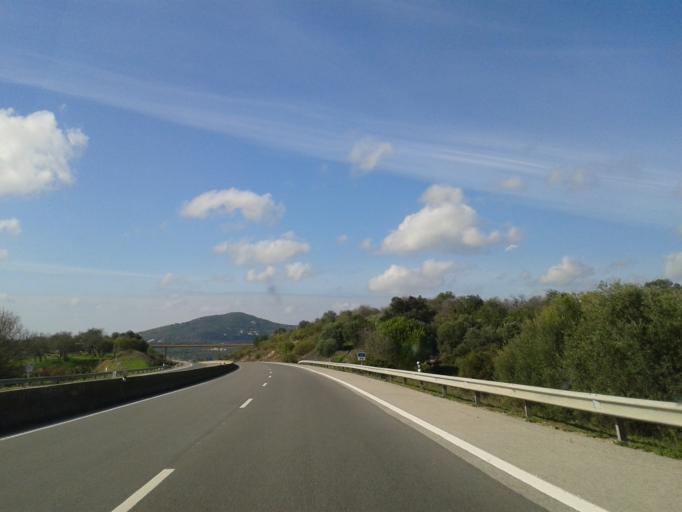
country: PT
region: Faro
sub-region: Sao Bras de Alportel
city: Sao Bras de Alportel
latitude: 37.0994
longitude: -7.8892
